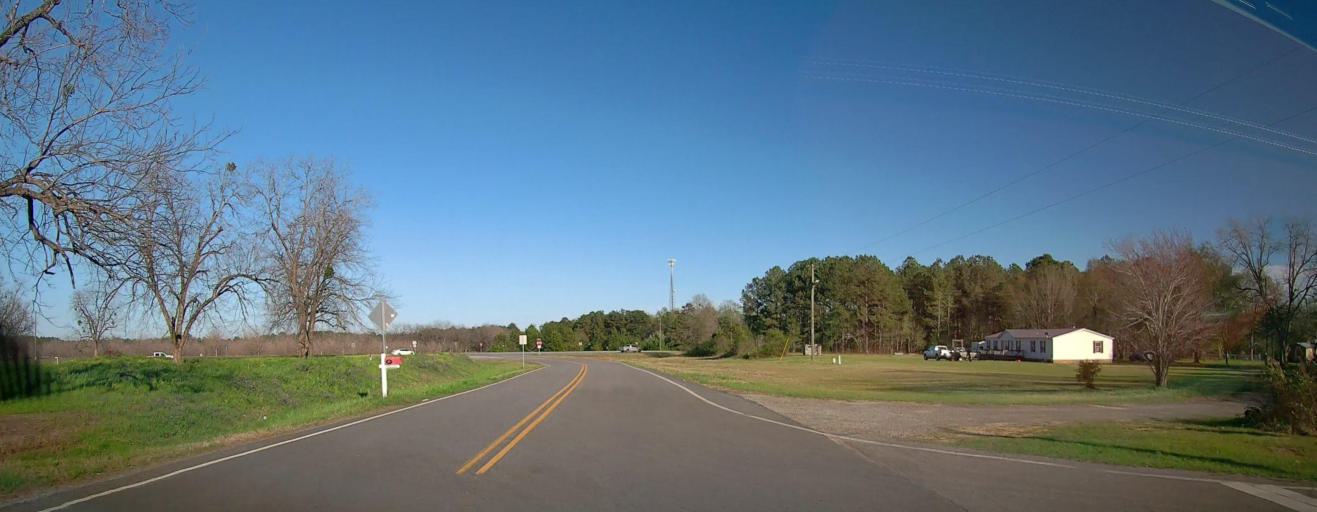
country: US
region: Georgia
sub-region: Pulaski County
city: Hawkinsville
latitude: 32.3471
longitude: -83.5768
